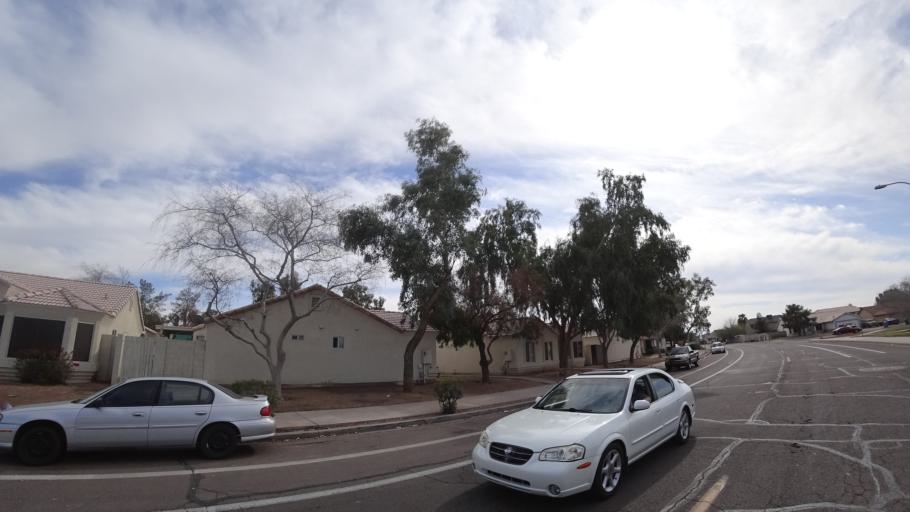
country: US
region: Arizona
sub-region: Maricopa County
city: Tolleson
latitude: 33.4721
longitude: -112.2431
